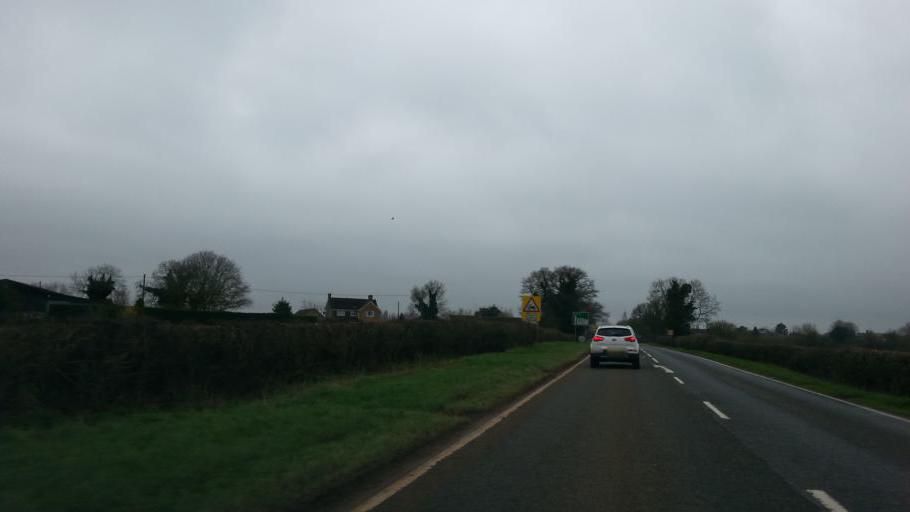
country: GB
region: England
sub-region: Oxfordshire
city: Adderbury
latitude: 52.0665
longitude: -1.2559
